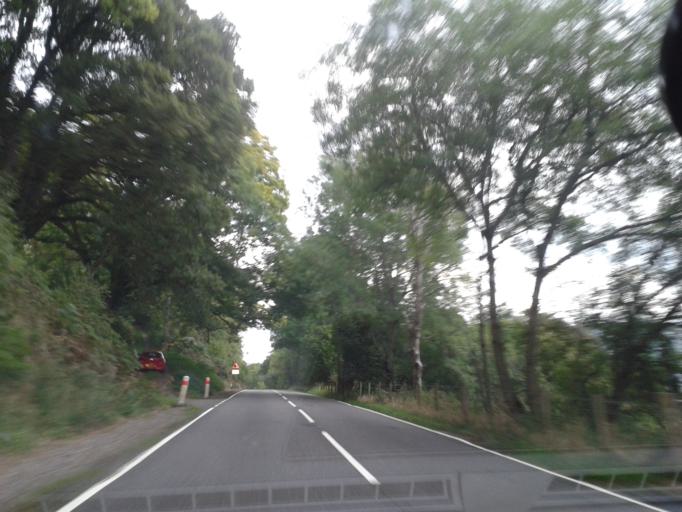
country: GB
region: Scotland
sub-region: Highland
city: Beauly
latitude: 57.3371
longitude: -4.4429
